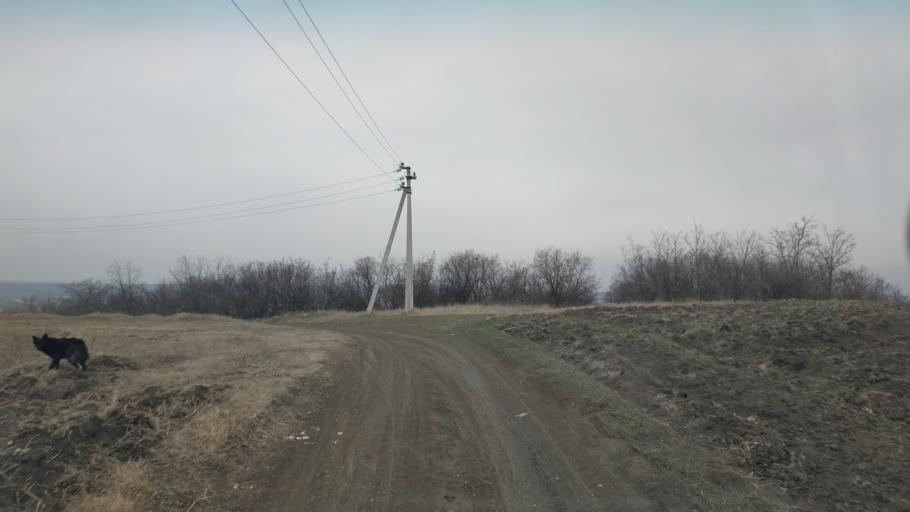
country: MD
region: Chisinau
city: Singera
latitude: 46.8223
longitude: 28.9804
